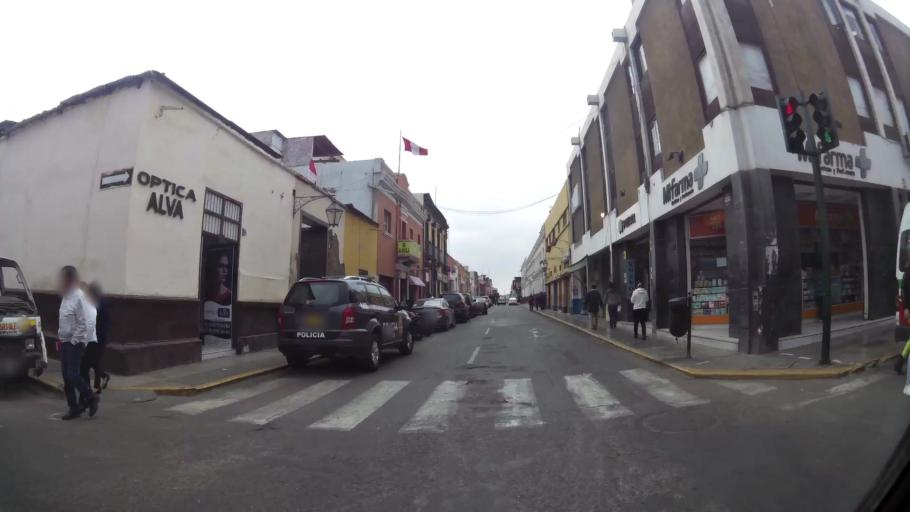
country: PE
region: La Libertad
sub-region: Provincia de Trujillo
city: Trujillo
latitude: -8.1134
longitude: -79.0262
